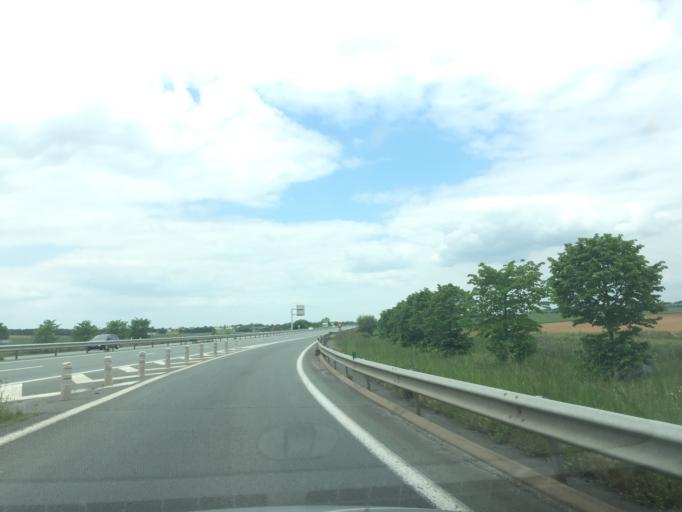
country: FR
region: Poitou-Charentes
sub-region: Departement des Deux-Sevres
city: La Creche
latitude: 46.3564
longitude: -0.3384
